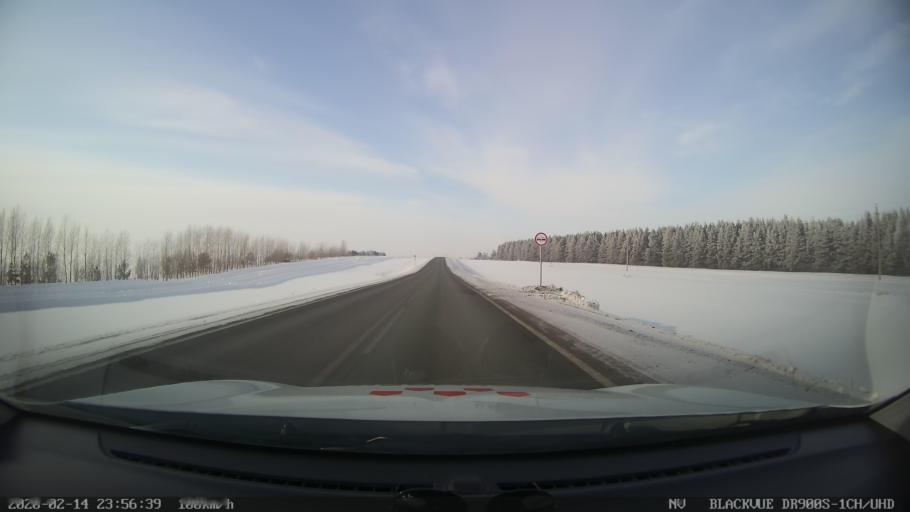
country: RU
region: Tatarstan
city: Kuybyshevskiy Zaton
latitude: 55.3271
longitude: 49.1262
